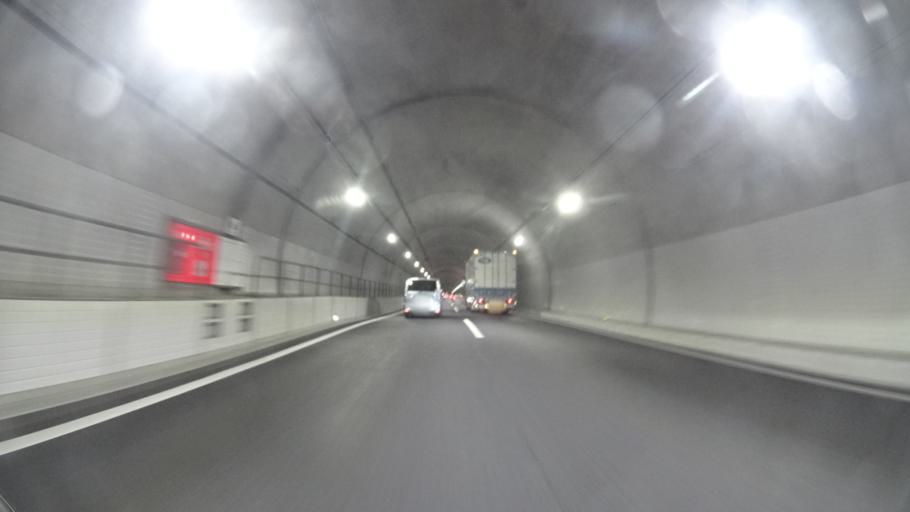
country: JP
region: Mie
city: Kameyama
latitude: 34.9335
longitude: 136.4314
